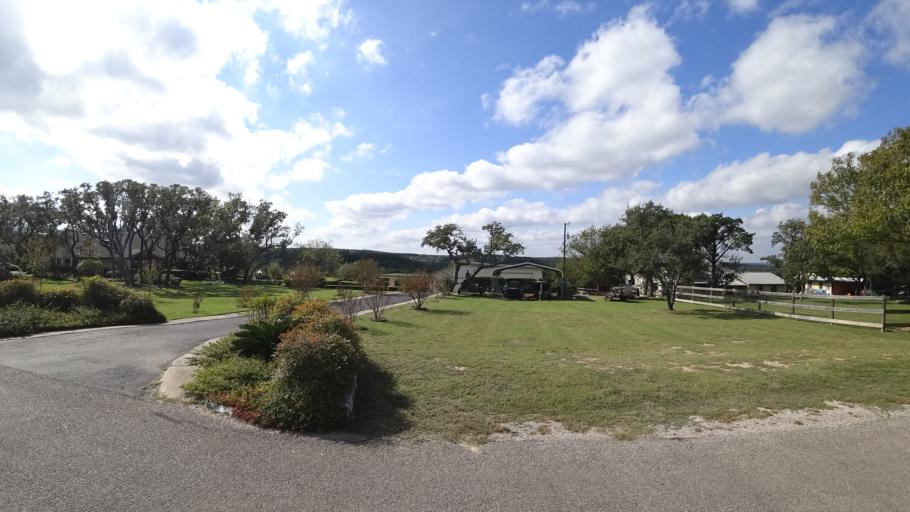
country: US
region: Texas
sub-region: Travis County
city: Bee Cave
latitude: 30.2543
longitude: -97.9341
